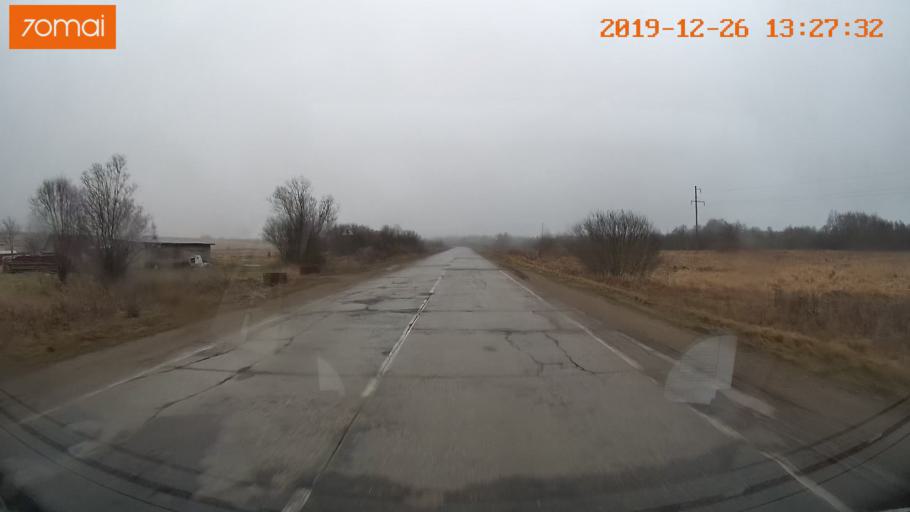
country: RU
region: Vologda
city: Cherepovets
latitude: 58.8529
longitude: 38.2410
